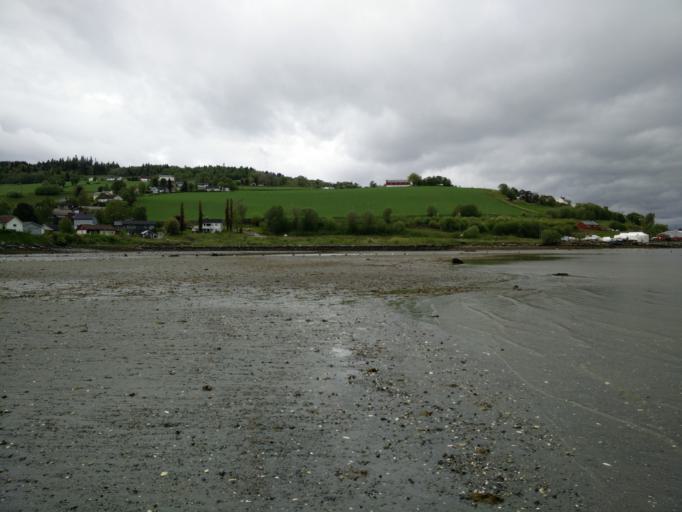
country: NO
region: Sor-Trondelag
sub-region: Skaun
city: Borsa
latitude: 63.3278
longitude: 10.0750
